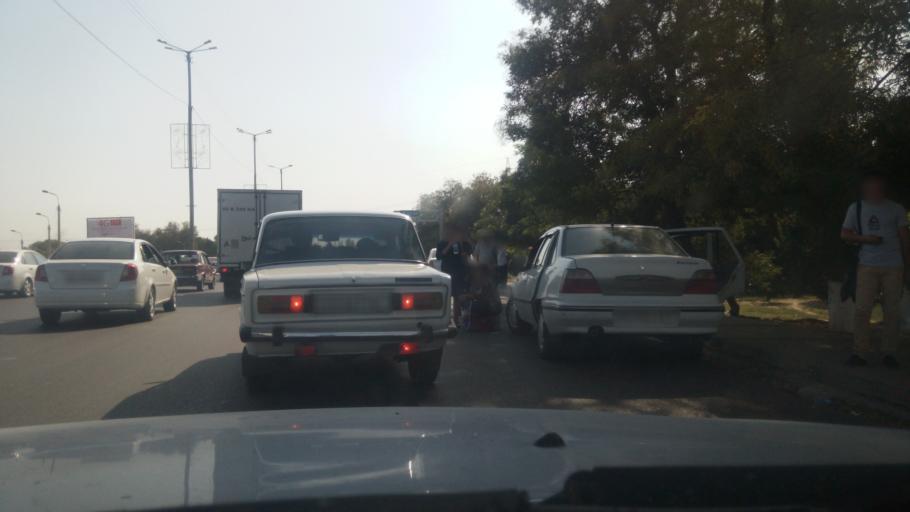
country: UZ
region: Toshkent Shahri
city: Tashkent
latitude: 41.2399
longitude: 69.1689
